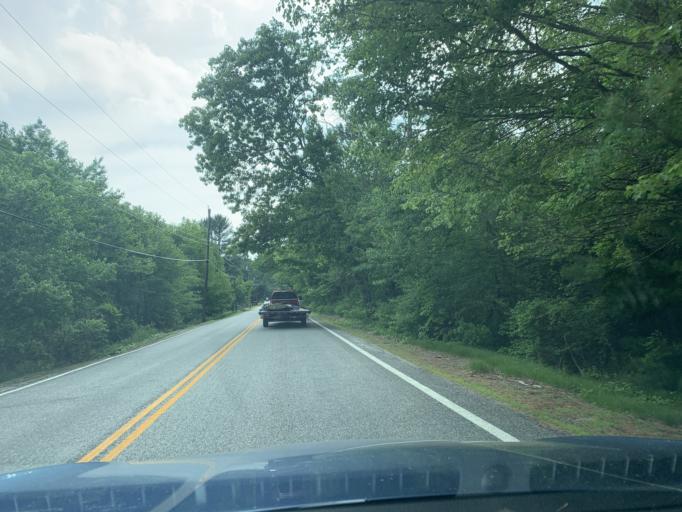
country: US
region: Rhode Island
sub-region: Kent County
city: Coventry
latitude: 41.7008
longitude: -71.7822
